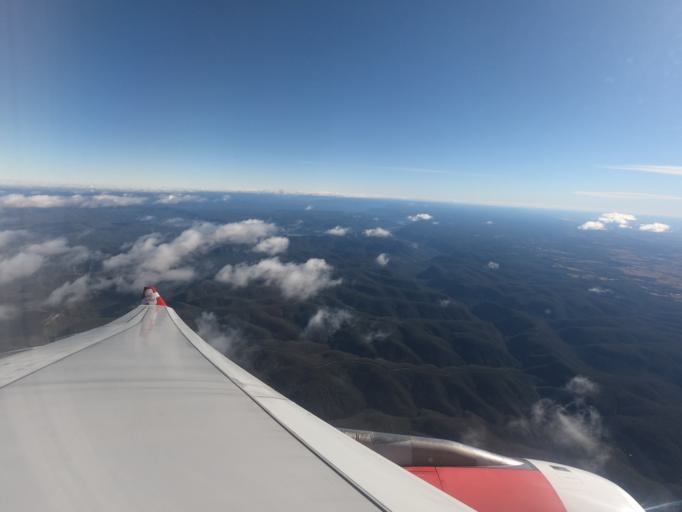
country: AU
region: New South Wales
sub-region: Wollondilly
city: Buxton
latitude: -34.2677
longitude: 150.4563
